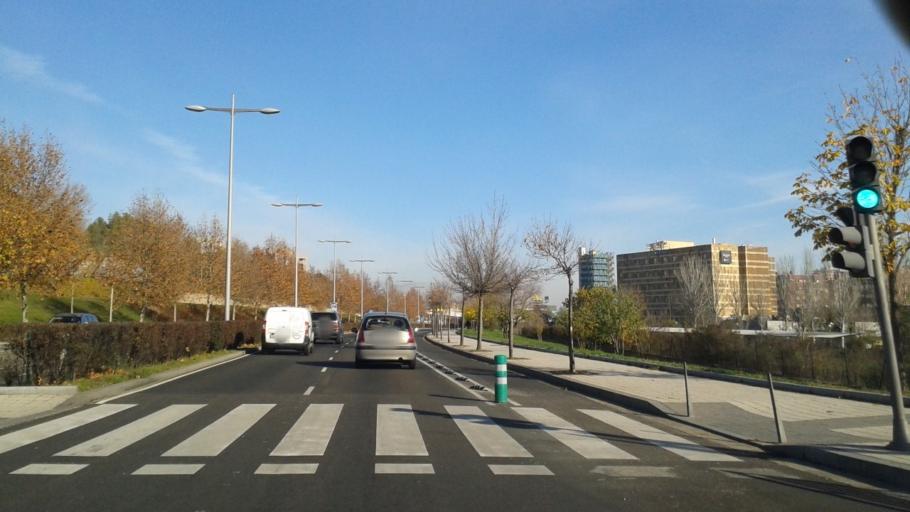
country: ES
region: Castille and Leon
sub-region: Provincia de Valladolid
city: Valladolid
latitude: 41.6341
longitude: -4.7494
